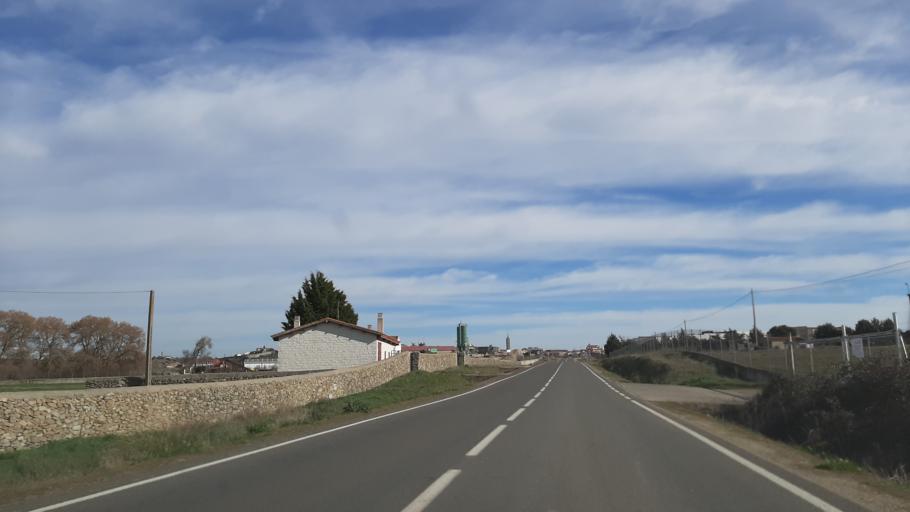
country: ES
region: Castille and Leon
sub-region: Provincia de Salamanca
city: Ledesma
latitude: 41.0930
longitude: -6.0171
